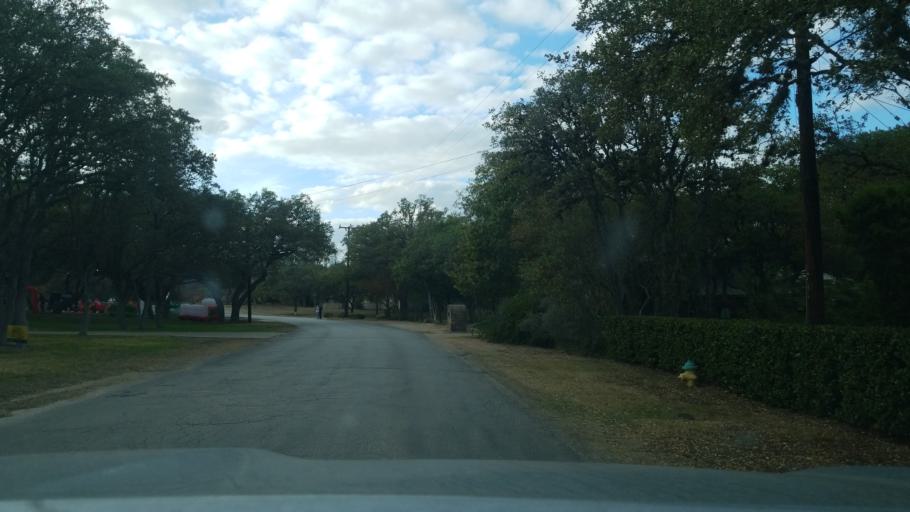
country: US
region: Texas
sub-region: Bexar County
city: Hollywood Park
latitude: 29.5950
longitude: -98.4778
